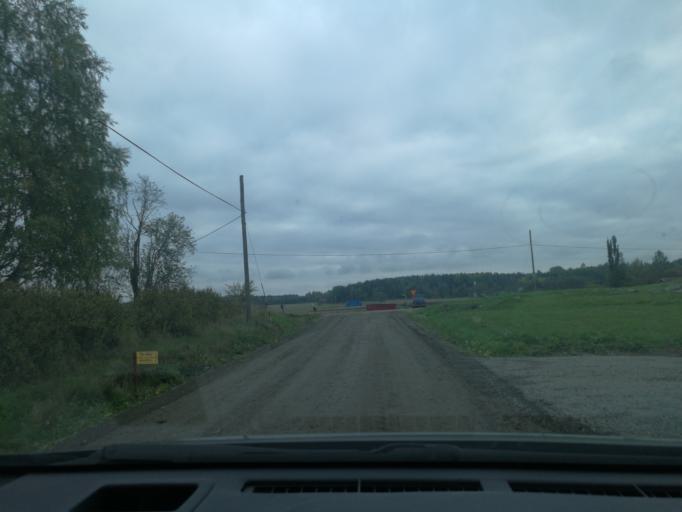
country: SE
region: Vaestmanland
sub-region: Vasteras
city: Tillberga
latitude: 59.7365
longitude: 16.7042
